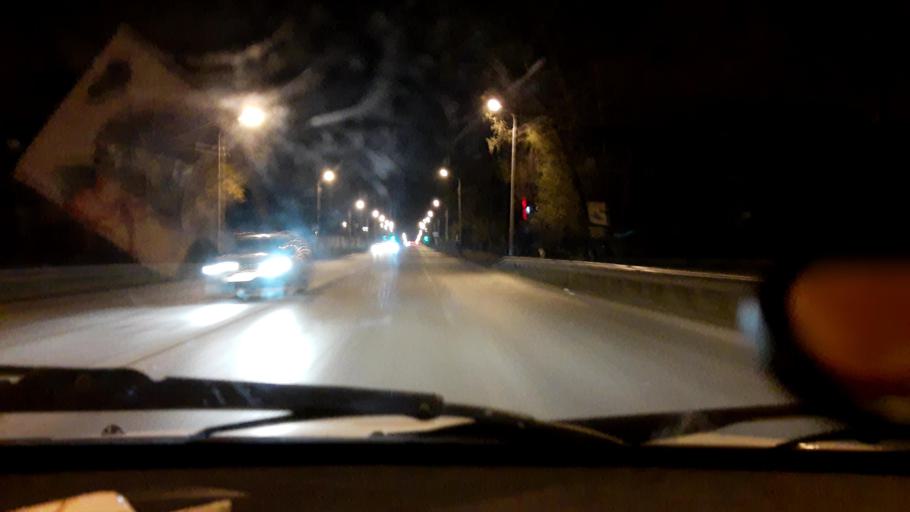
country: RU
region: Bashkortostan
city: Iglino
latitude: 54.7850
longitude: 56.2209
